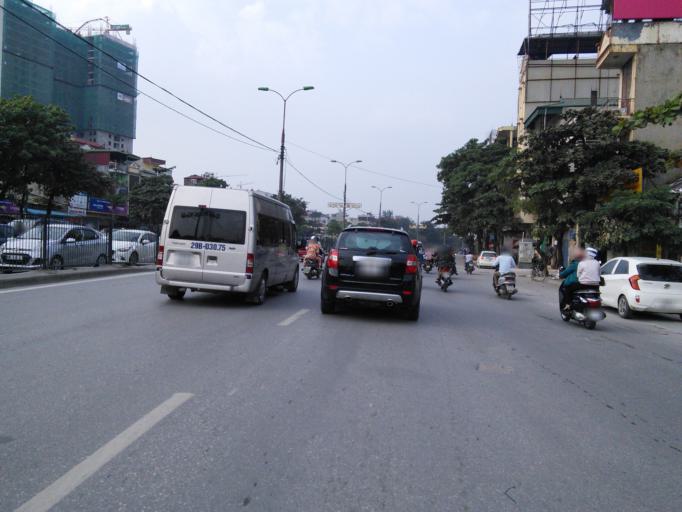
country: VN
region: Ha Noi
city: Van Dien
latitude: 20.9712
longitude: 105.8410
